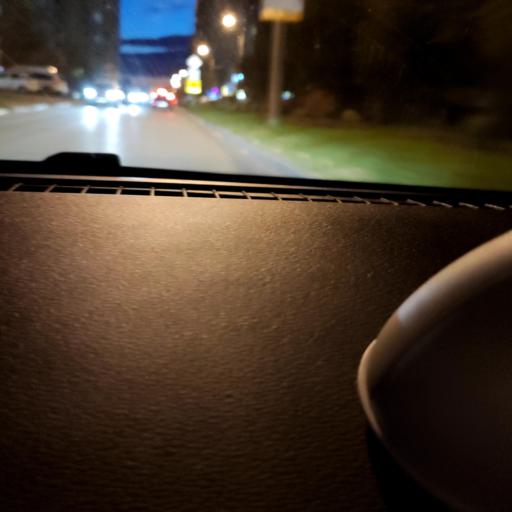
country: RU
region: Samara
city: Samara
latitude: 53.2241
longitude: 50.1968
